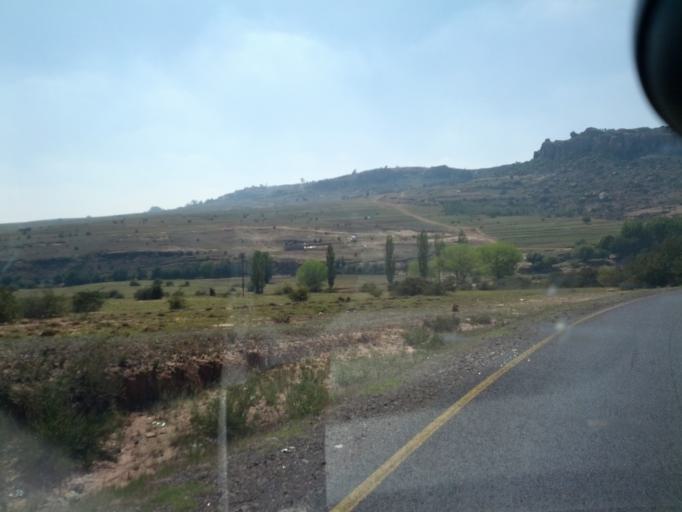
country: LS
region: Berea
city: Teyateyaneng
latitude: -29.1380
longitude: 27.7058
